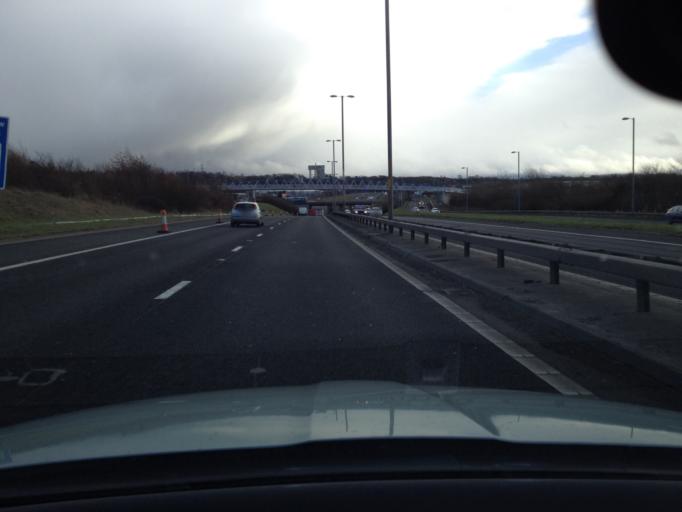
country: GB
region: Scotland
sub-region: Edinburgh
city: Newbridge
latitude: 55.9421
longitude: -3.4039
